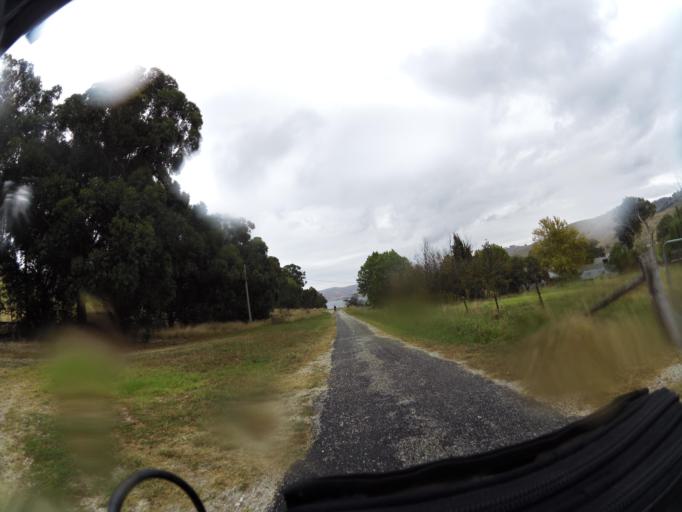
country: AU
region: New South Wales
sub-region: Albury Municipality
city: East Albury
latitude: -36.2166
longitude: 147.2275
